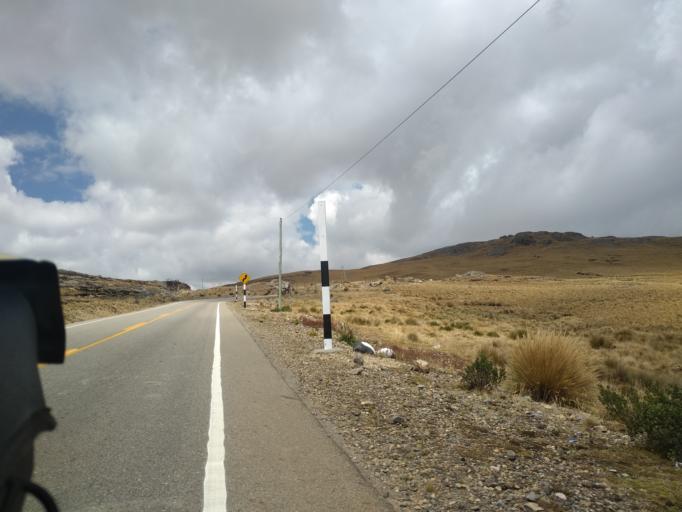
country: PE
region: La Libertad
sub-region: Provincia de Santiago de Chuco
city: Quiruvilca
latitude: -7.9484
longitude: -78.1909
